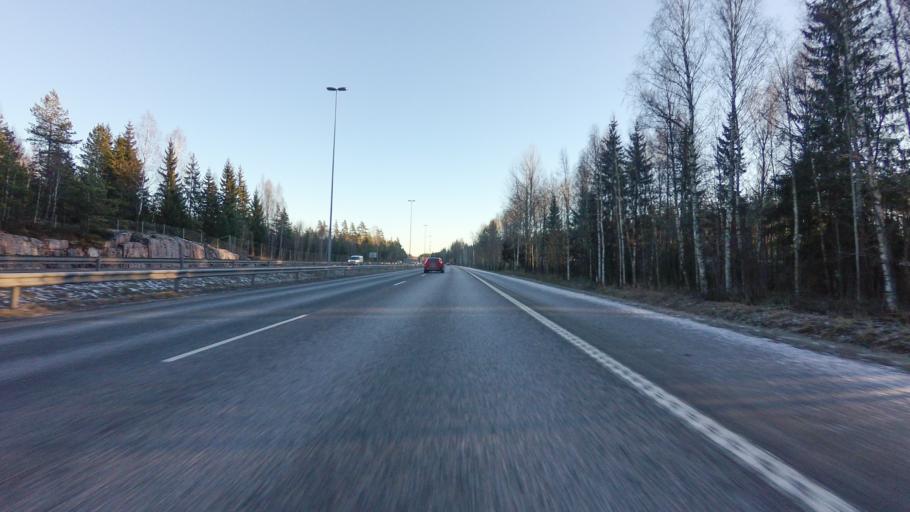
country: FI
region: Uusimaa
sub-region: Helsinki
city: Espoo
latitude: 60.2478
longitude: 24.5453
